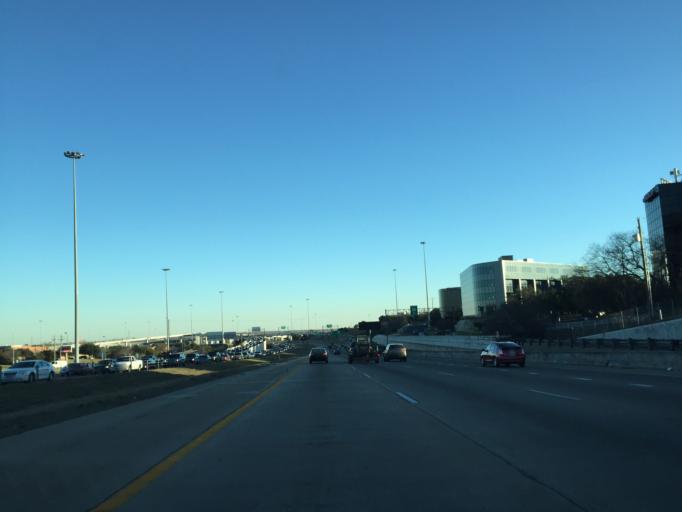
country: US
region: Texas
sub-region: Williamson County
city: Jollyville
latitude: 30.3870
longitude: -97.7440
